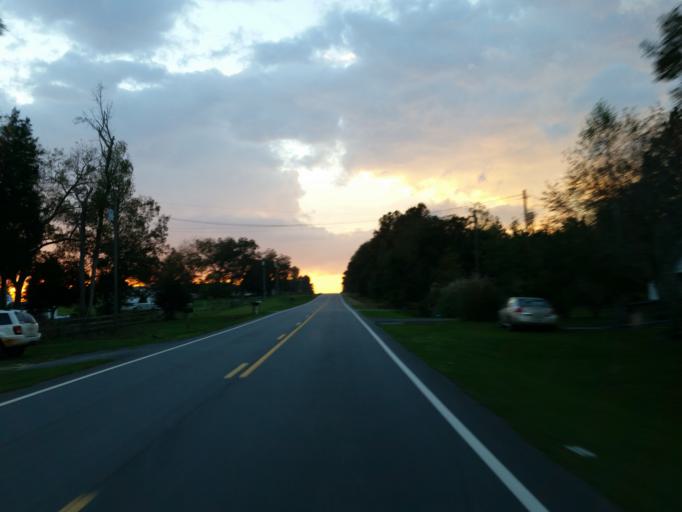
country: US
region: Georgia
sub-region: Pulaski County
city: Hawkinsville
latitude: 32.2081
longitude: -83.5531
